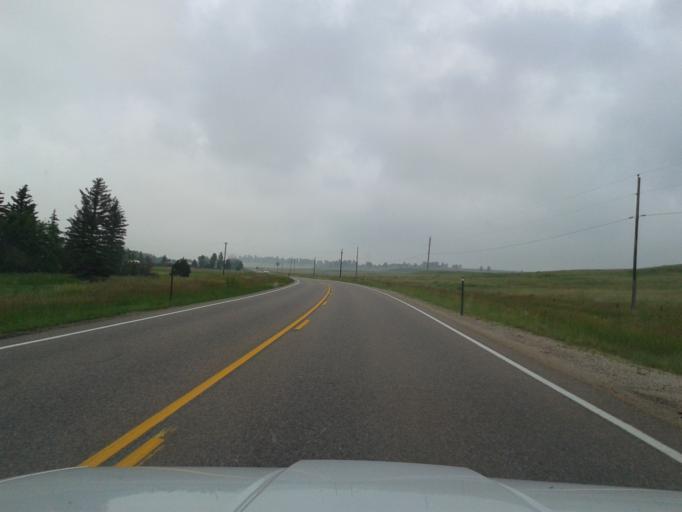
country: US
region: Colorado
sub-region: Elbert County
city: Elizabeth
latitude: 39.2369
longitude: -104.6962
